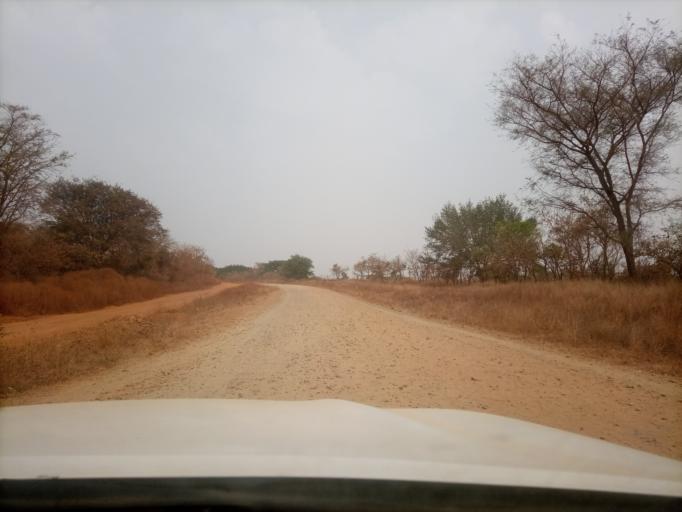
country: ET
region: Oromiya
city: Mendi
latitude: 10.1638
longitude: 35.1020
